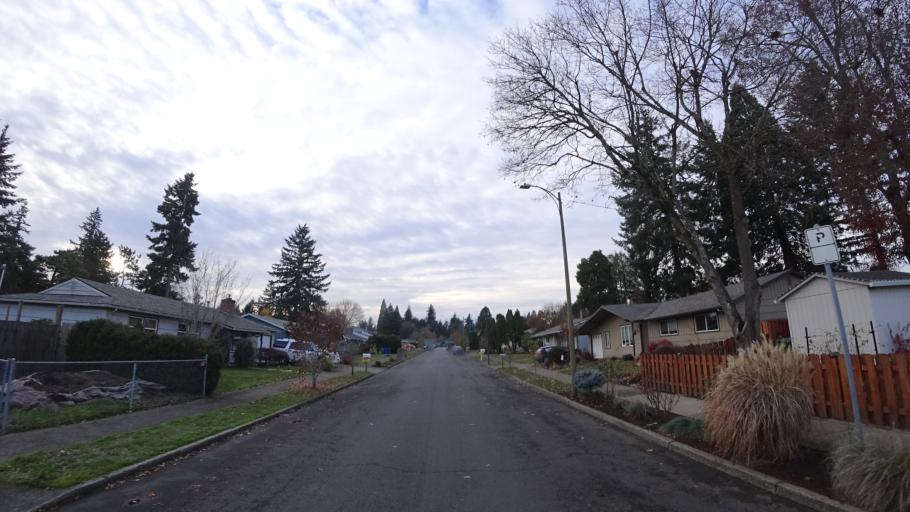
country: US
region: Oregon
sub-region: Multnomah County
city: Lents
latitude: 45.5146
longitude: -122.5161
